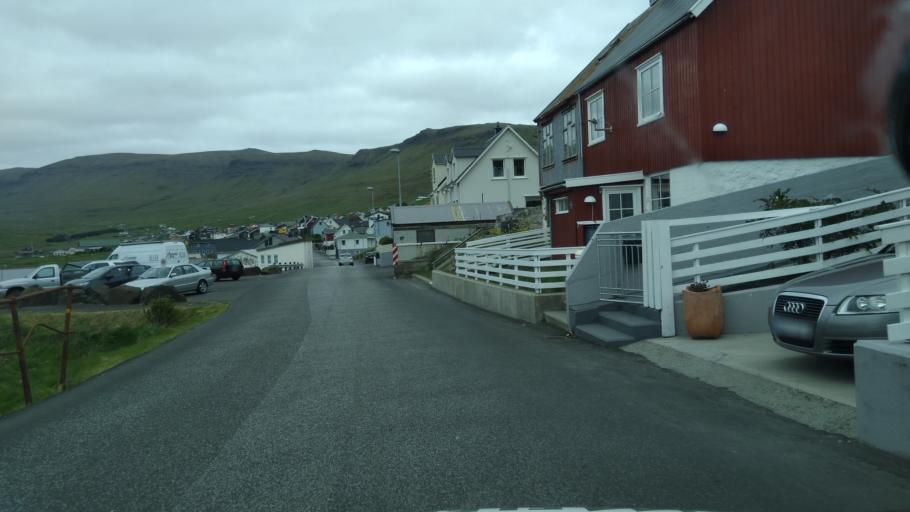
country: FO
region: Suduroy
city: Tvoroyri
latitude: 61.5615
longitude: -6.8277
